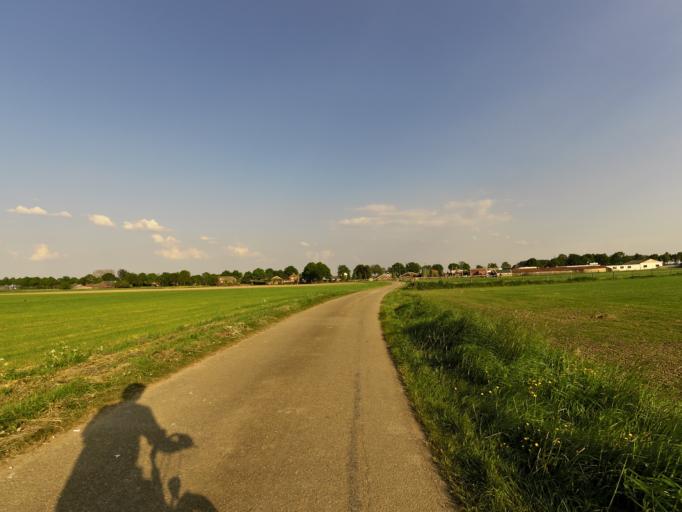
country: NL
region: Gelderland
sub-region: Gemeente Montferland
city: s-Heerenberg
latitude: 51.9063
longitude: 6.3116
